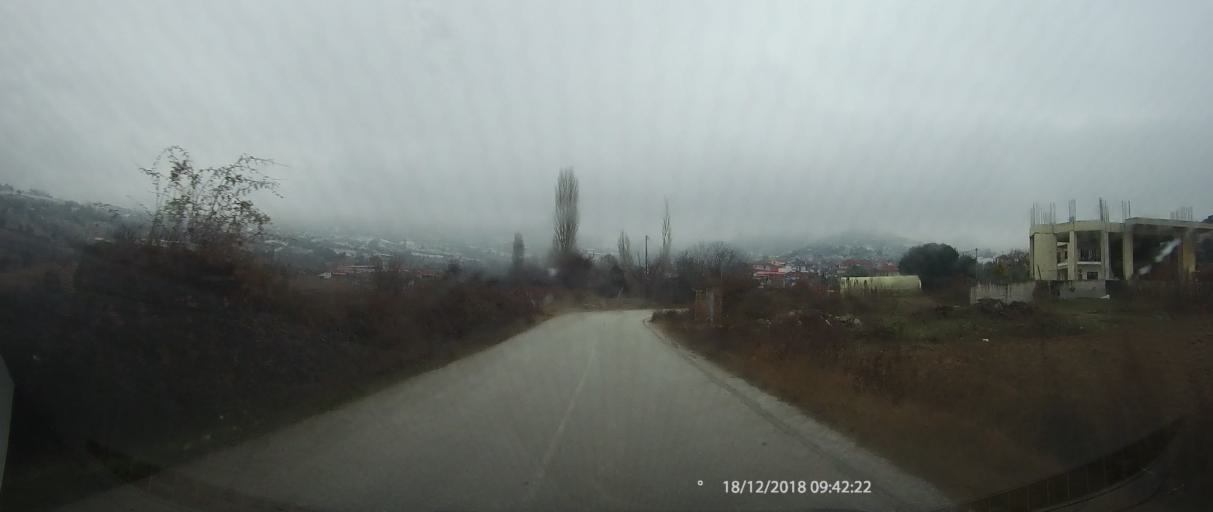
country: GR
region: Thessaly
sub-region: Nomos Larisis
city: Livadi
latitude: 40.0199
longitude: 22.2371
